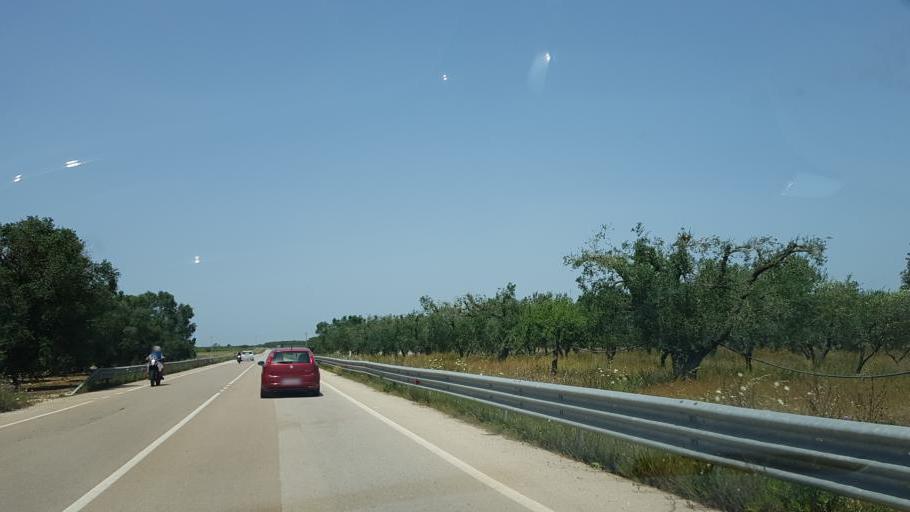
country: IT
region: Apulia
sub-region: Provincia di Brindisi
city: San Pancrazio Salentino
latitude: 40.4754
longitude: 17.8373
